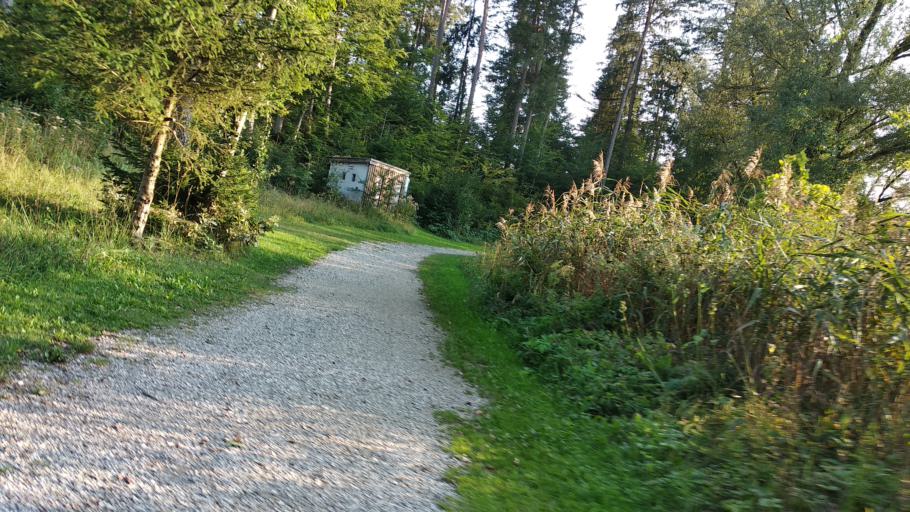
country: DE
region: Bavaria
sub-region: Upper Bavaria
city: Seeon-Seebruck
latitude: 47.9870
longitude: 12.4462
